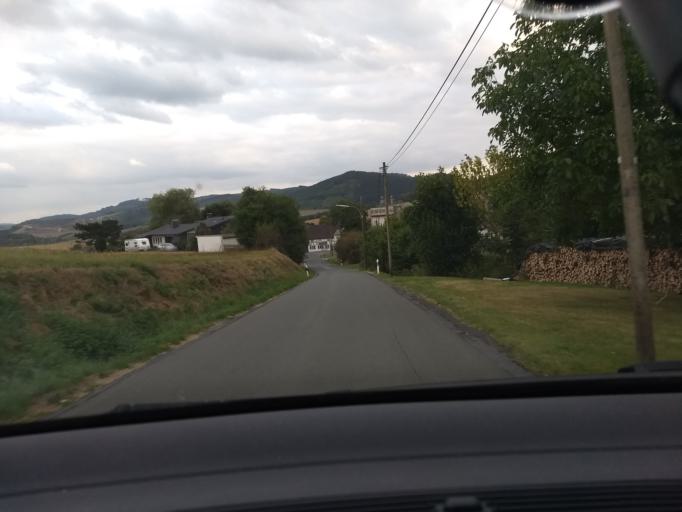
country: DE
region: North Rhine-Westphalia
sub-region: Regierungsbezirk Arnsberg
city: Arnsberg
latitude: 51.3346
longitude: 8.1277
